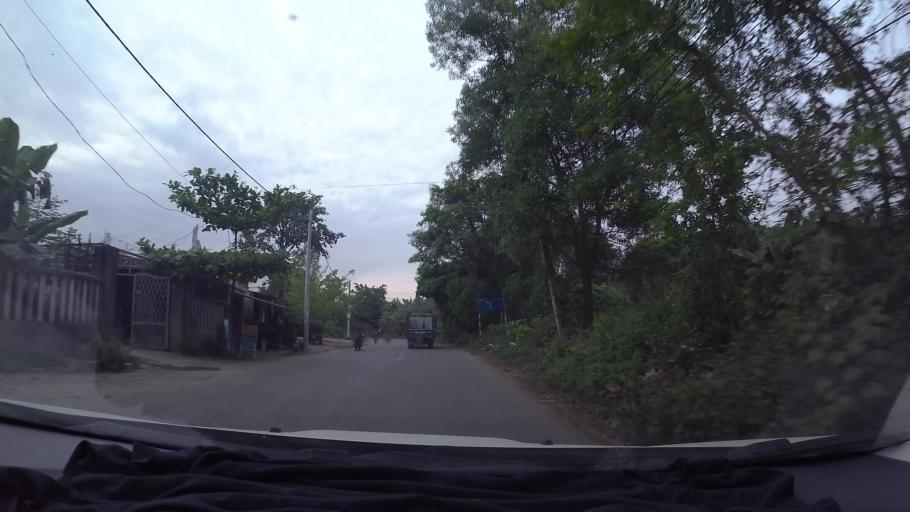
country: VN
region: Da Nang
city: Lien Chieu
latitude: 16.0586
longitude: 108.0979
